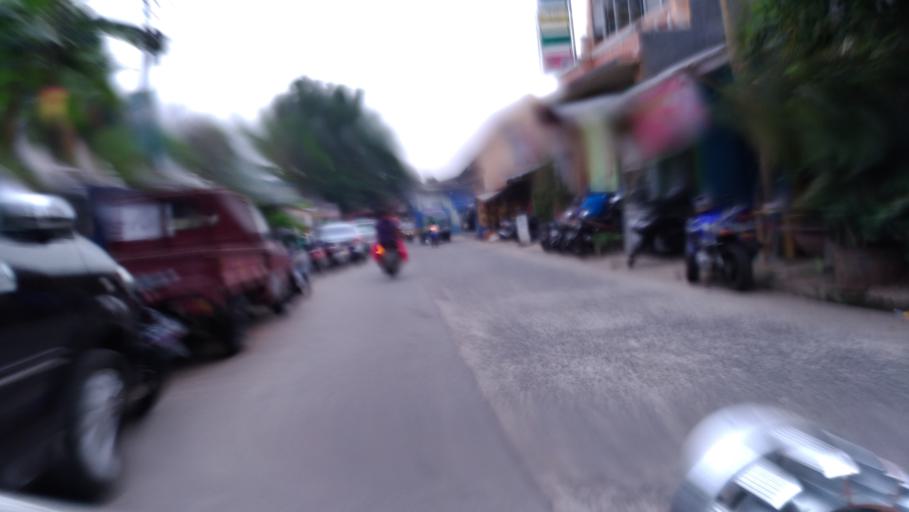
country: ID
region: West Java
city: Depok
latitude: -6.3561
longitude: 106.8534
